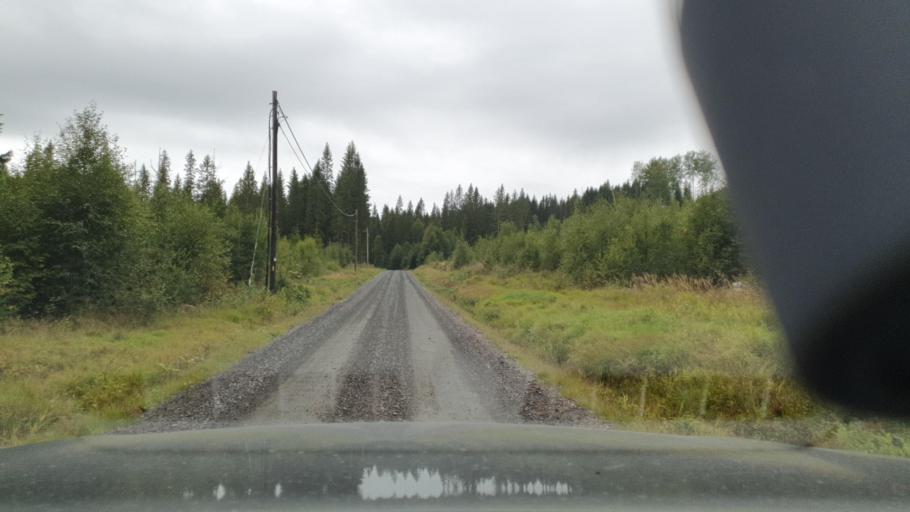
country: SE
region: Vaermland
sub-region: Torsby Kommun
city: Torsby
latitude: 60.3435
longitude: 12.6248
